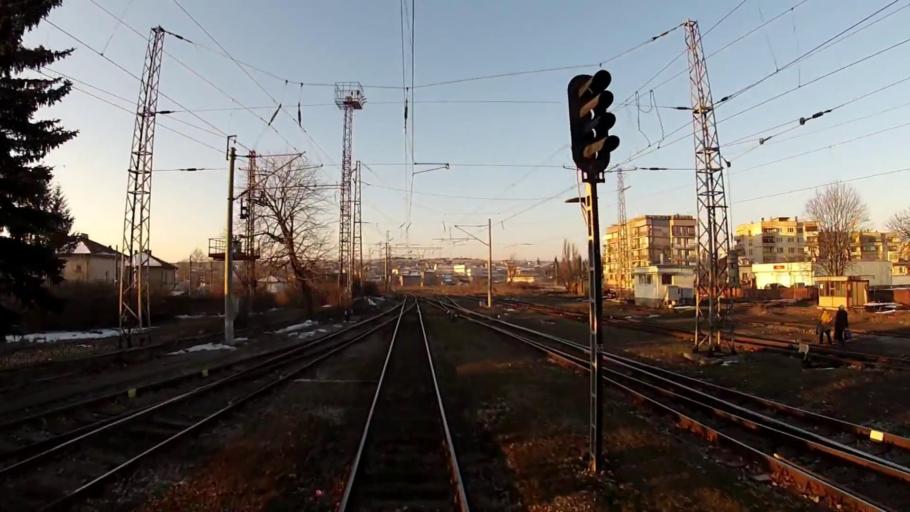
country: BG
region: Sofiya
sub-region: Obshtina Dragoman
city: Dragoman
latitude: 42.9179
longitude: 22.9310
